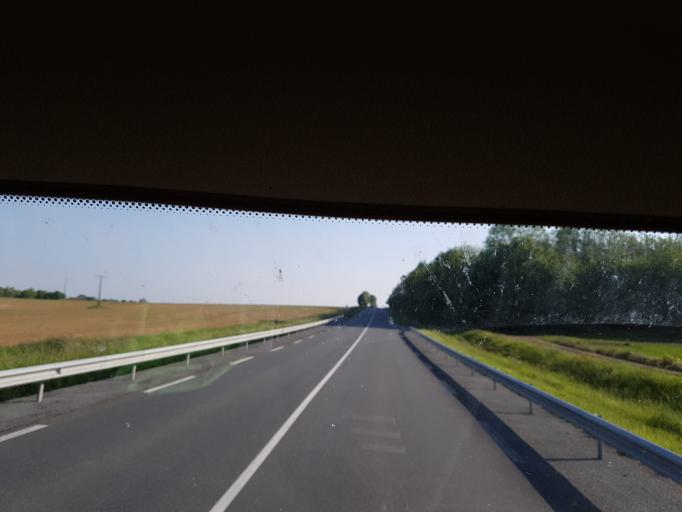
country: FR
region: Picardie
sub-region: Departement de la Somme
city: Crecy-en-Ponthieu
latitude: 50.1768
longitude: 1.8708
